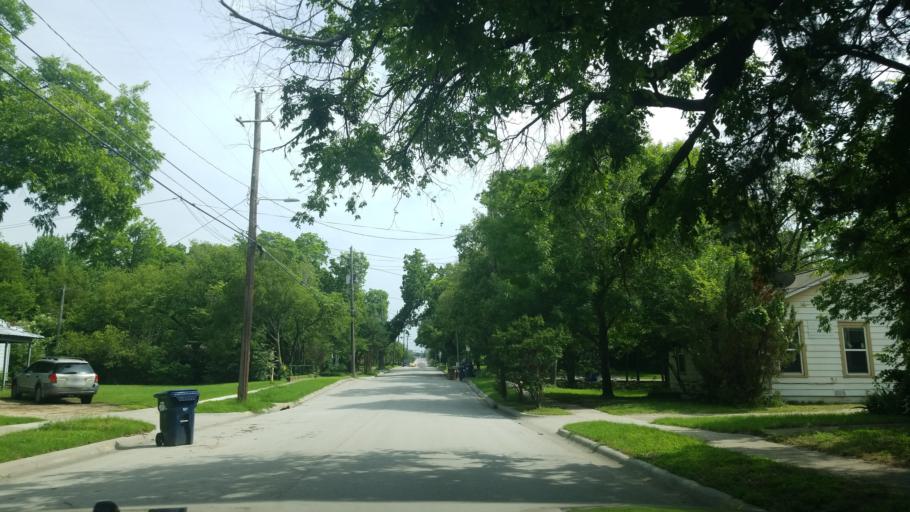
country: US
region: Texas
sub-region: Denton County
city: Denton
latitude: 33.2227
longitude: -97.1350
